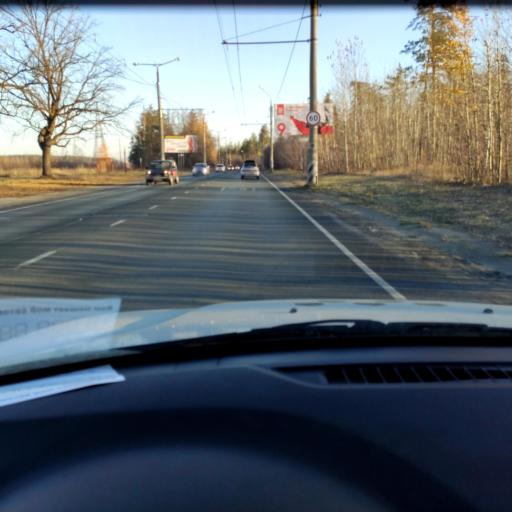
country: RU
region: Samara
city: Tol'yatti
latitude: 53.4872
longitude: 49.3826
